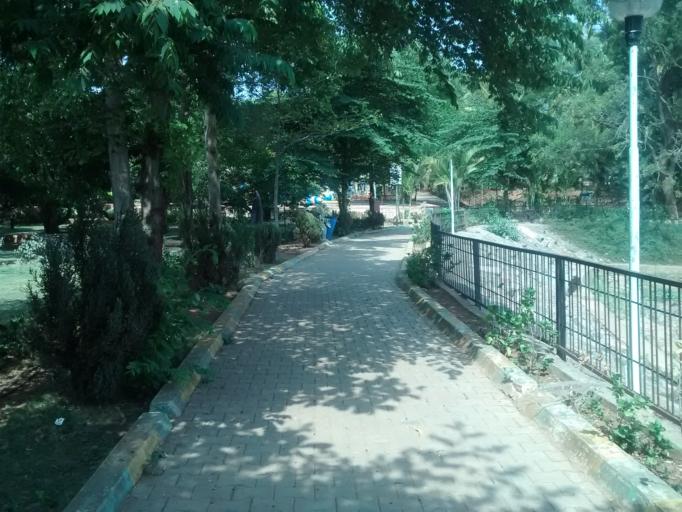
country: IN
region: Karnataka
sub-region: Dharwad
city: Hubli
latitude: 15.4655
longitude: 74.9865
